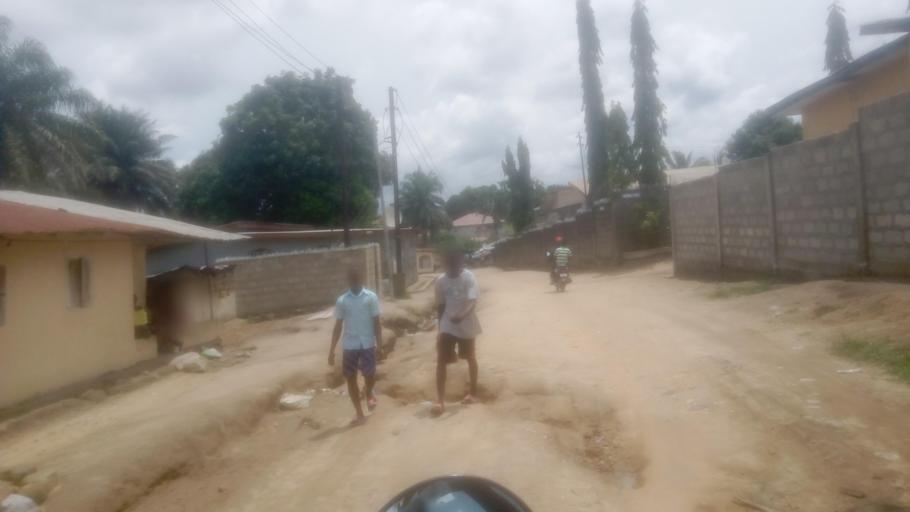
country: SL
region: Southern Province
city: Bo
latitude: 7.9543
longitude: -11.7153
